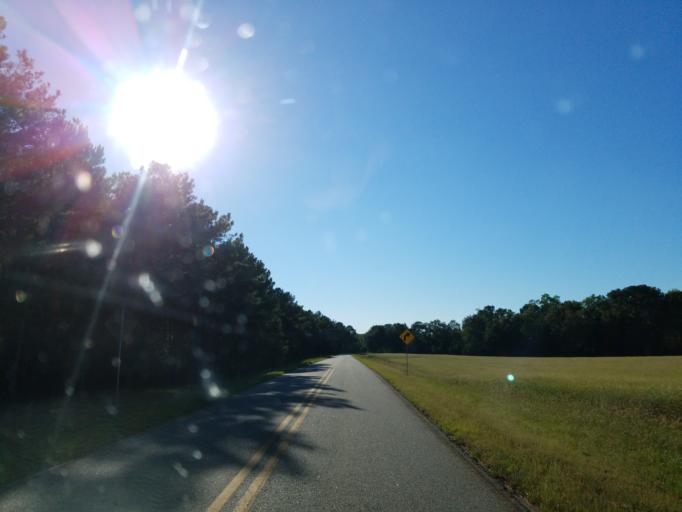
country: US
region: Georgia
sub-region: Lee County
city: Leesburg
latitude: 31.9136
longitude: -84.0348
